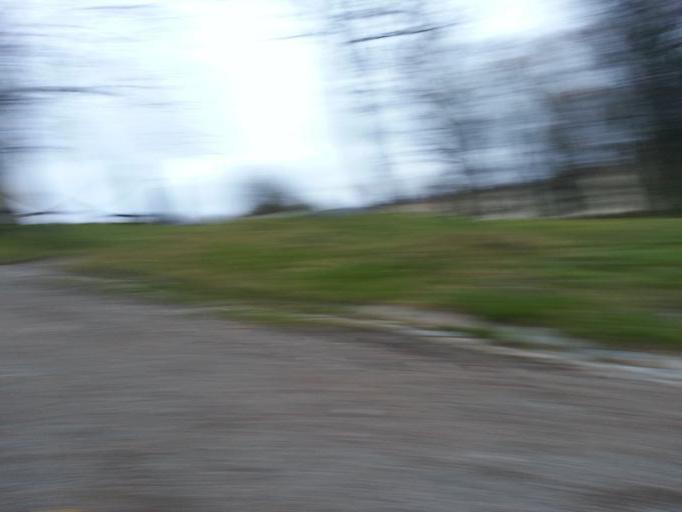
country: FI
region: Uusimaa
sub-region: Helsinki
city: Helsinki
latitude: 60.1474
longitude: 24.9859
